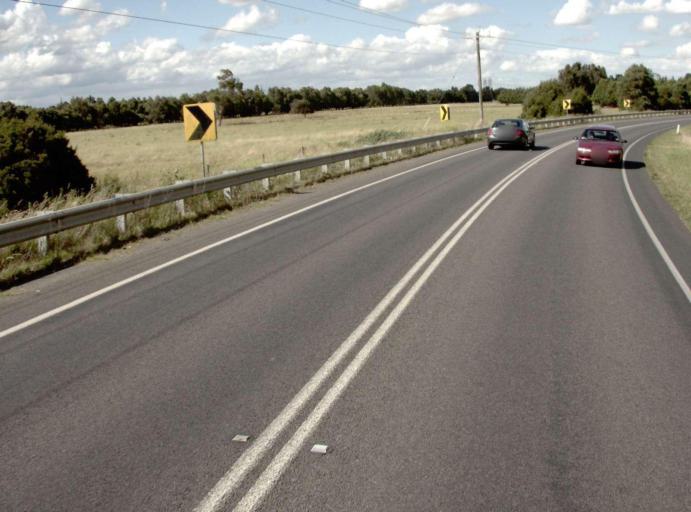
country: AU
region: Victoria
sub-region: Latrobe
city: Morwell
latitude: -38.2954
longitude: 146.4236
